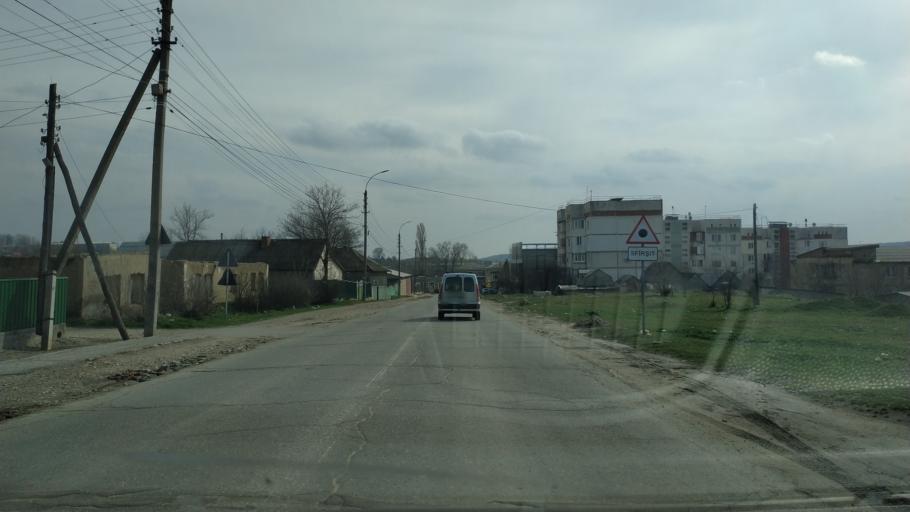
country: MD
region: Gagauzia
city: Vulcanesti
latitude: 45.6899
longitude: 28.4060
